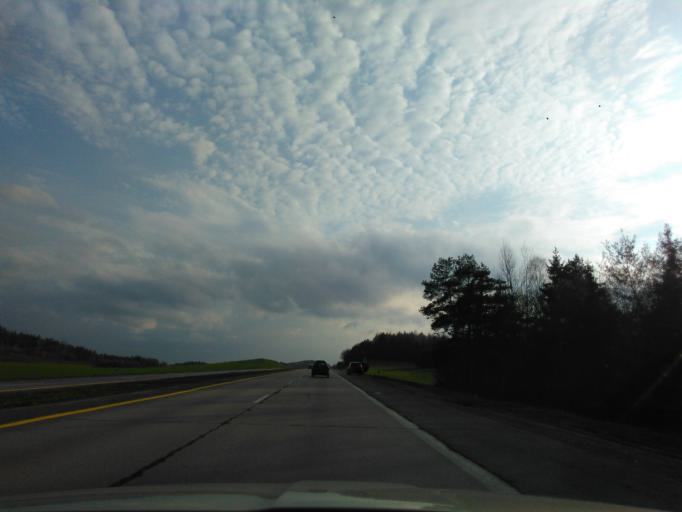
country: BY
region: Minsk
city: Astrashytski Haradok
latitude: 54.0750
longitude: 27.7343
